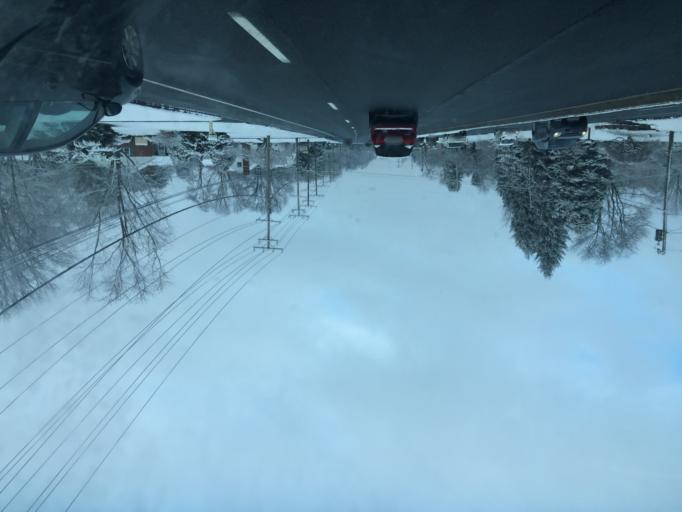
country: US
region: Maryland
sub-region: Harford County
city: Pleasant Hills
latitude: 39.4948
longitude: -76.3959
